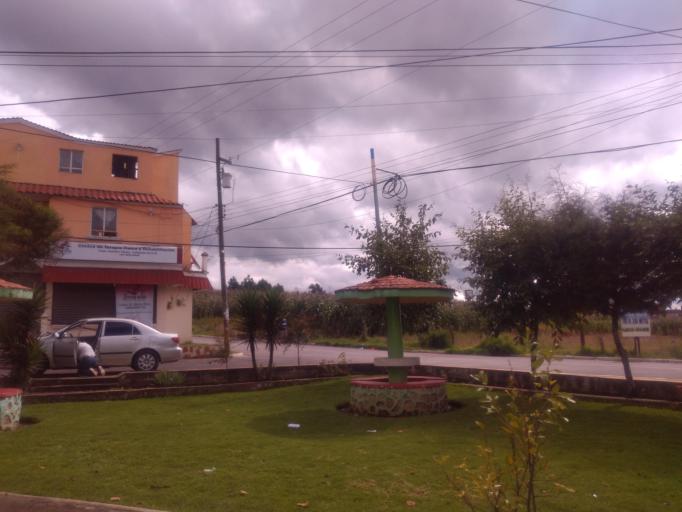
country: GT
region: Quetzaltenango
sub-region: Municipio de La Esperanza
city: La Esperanza
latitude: 14.8683
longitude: -91.5590
